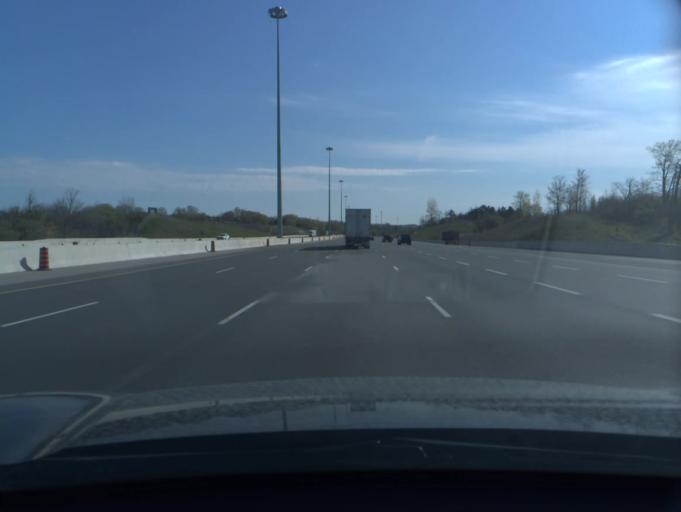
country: CA
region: Ontario
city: North Perth
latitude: 43.8143
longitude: -80.9998
